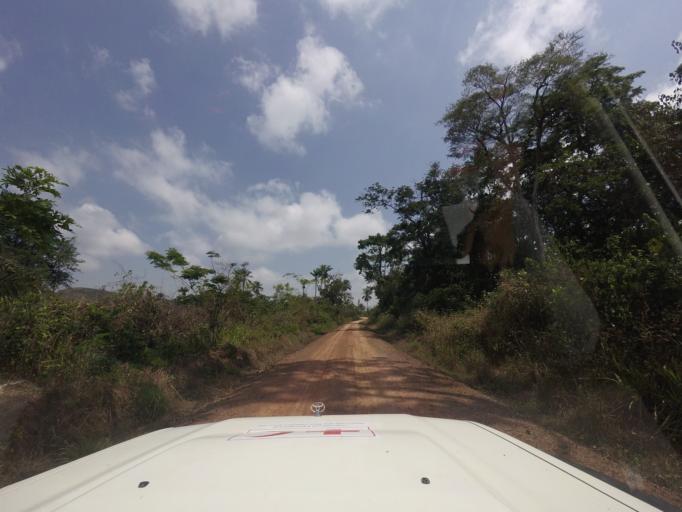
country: LR
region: Lofa
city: Voinjama
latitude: 8.4688
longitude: -9.6650
